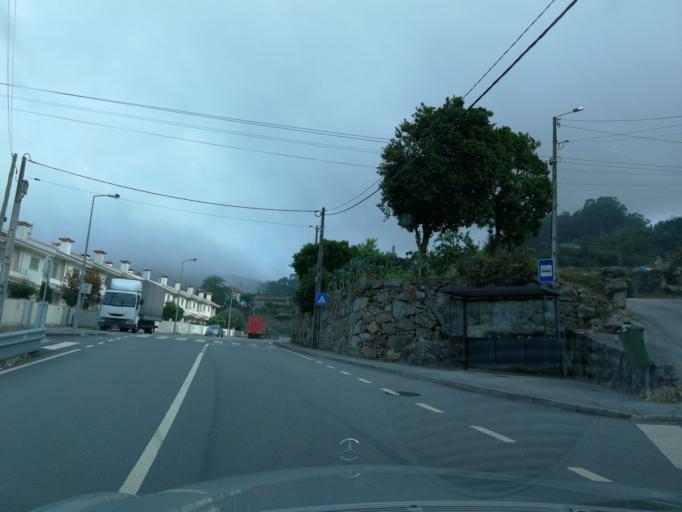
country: PT
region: Braga
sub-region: Guimaraes
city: Ponte
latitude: 41.5181
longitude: -8.3574
